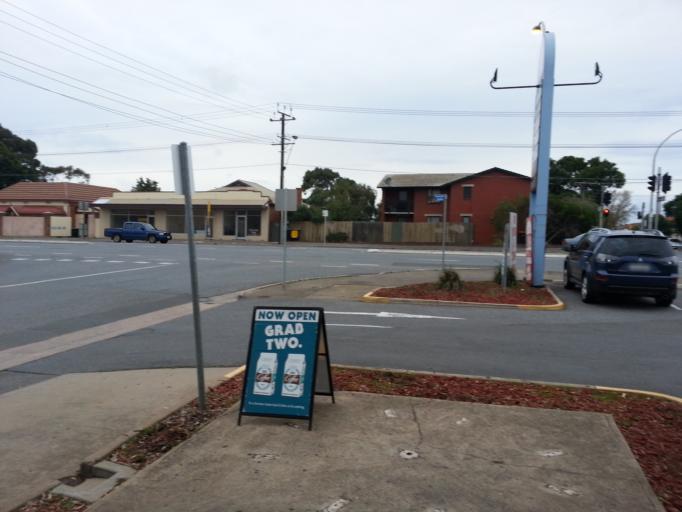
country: AU
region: South Australia
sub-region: Port Adelaide Enfield
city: Alberton
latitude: -34.8515
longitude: 138.5217
